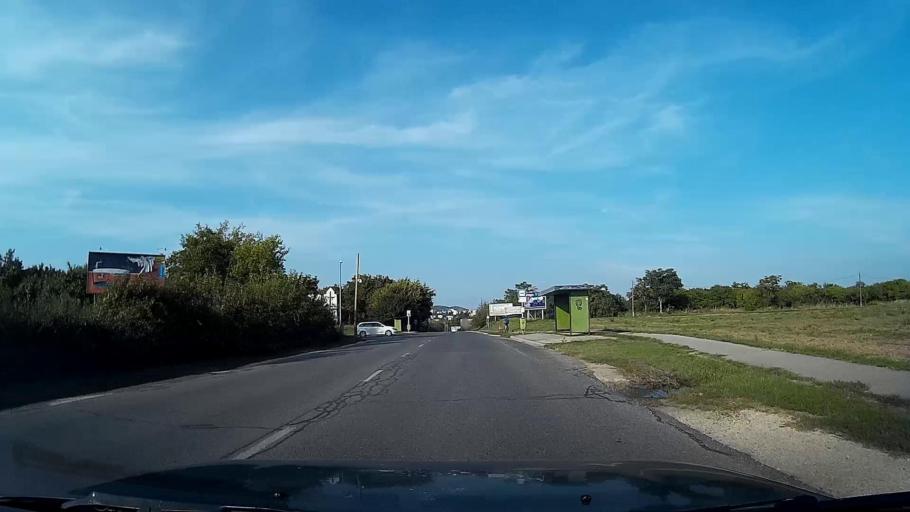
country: HU
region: Pest
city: Budaors
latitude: 47.4524
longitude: 18.9906
